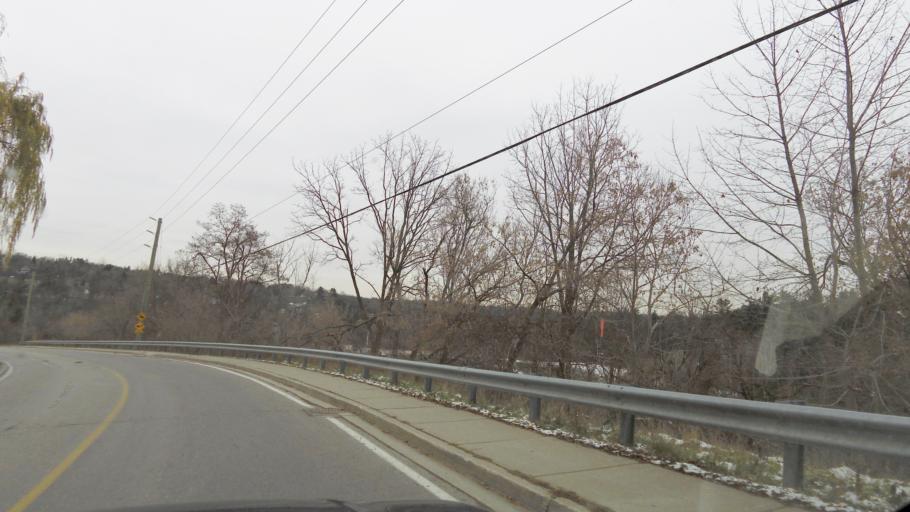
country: CA
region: Ontario
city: Vaughan
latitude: 43.8435
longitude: -79.6255
